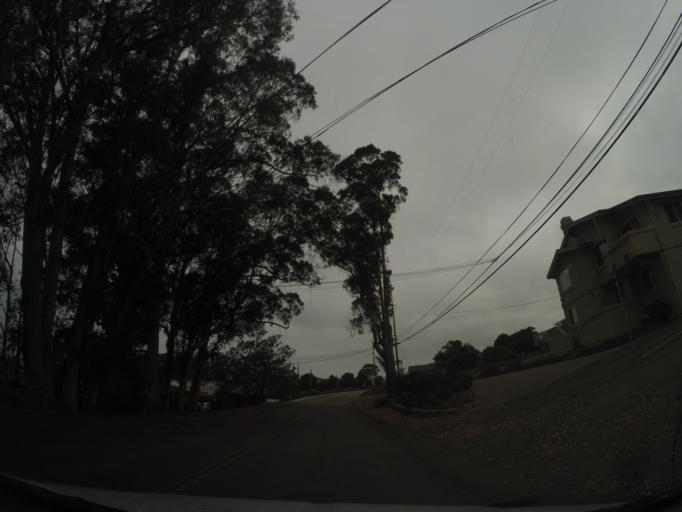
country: US
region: California
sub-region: San Luis Obispo County
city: Morro Bay
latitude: 35.3595
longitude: -120.8497
